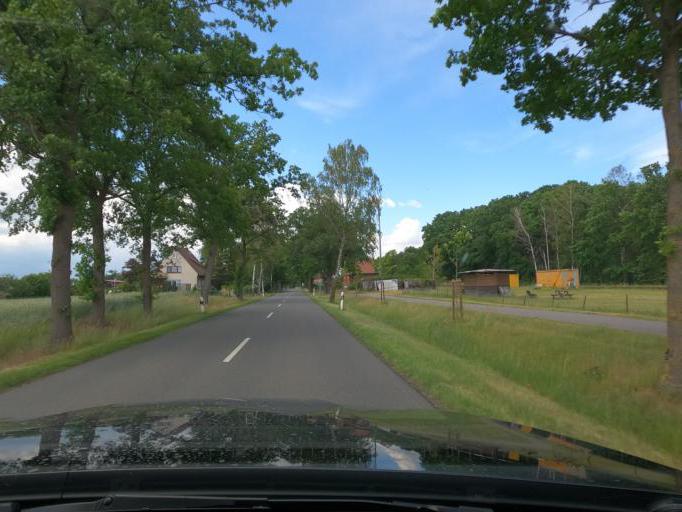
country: DE
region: Lower Saxony
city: Lindwedel
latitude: 52.6308
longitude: 9.6451
